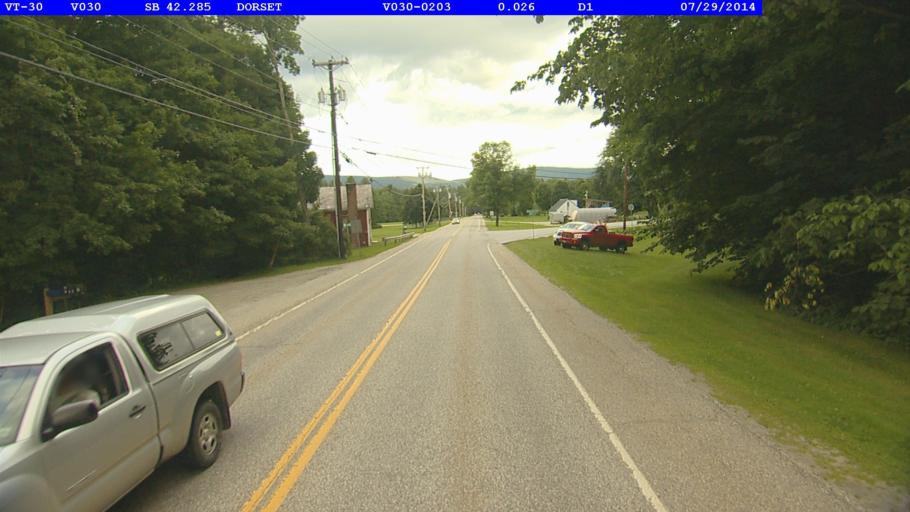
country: US
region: Vermont
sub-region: Bennington County
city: Manchester Center
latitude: 43.2129
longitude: -73.0675
